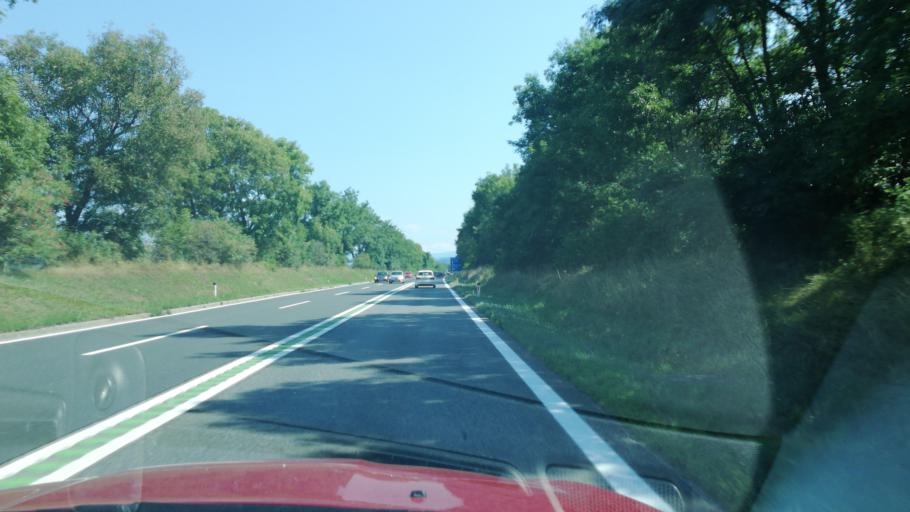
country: AT
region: Carinthia
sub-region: Politischer Bezirk Klagenfurt Land
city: Maria Saal
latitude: 46.6756
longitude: 14.3271
